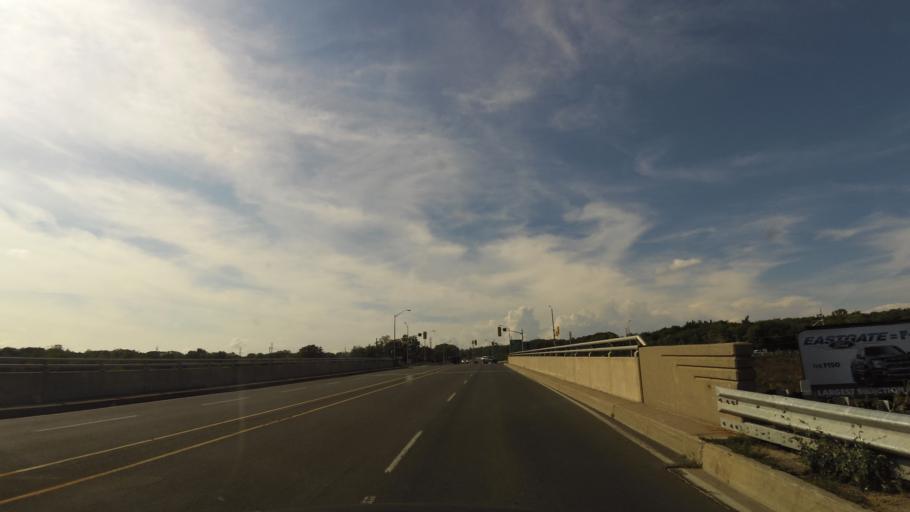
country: CA
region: Ontario
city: Hamilton
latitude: 43.3108
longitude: -79.8579
